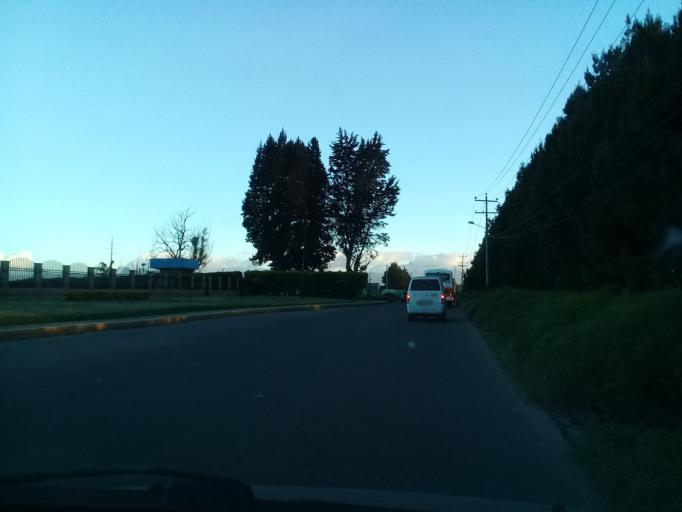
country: CO
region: Cundinamarca
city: Cota
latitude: 4.7702
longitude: -74.1575
